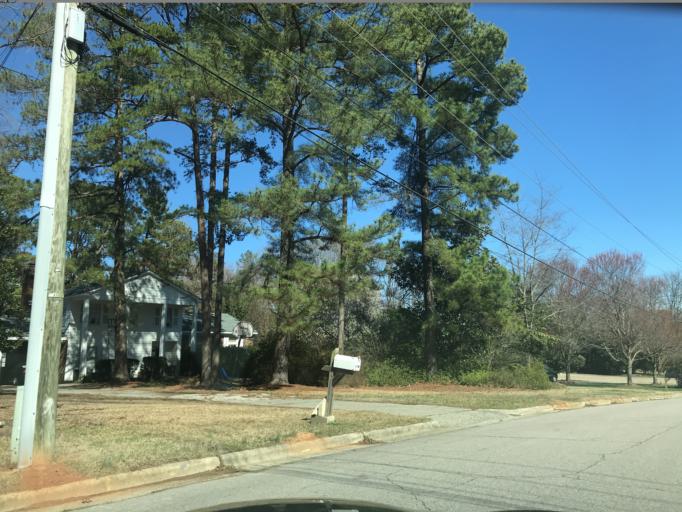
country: US
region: North Carolina
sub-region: Wake County
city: West Raleigh
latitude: 35.8518
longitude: -78.6393
